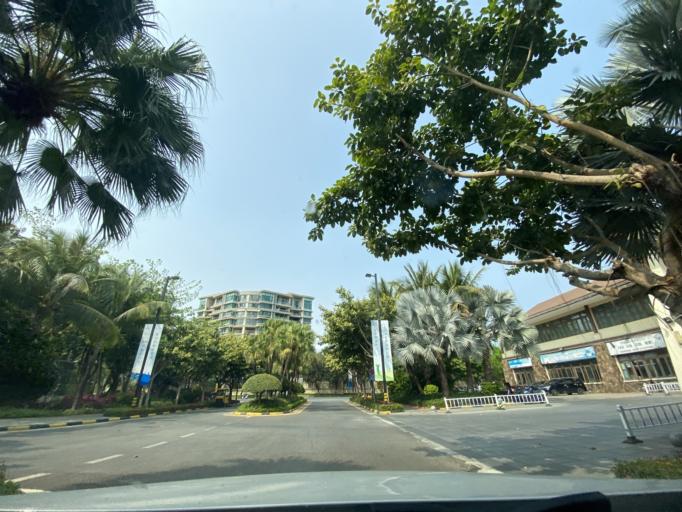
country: CN
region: Hainan
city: Yingzhou
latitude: 18.4020
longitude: 109.8466
